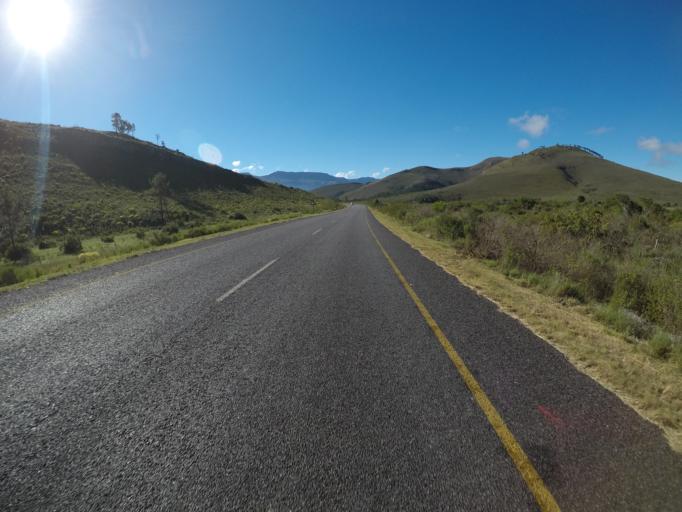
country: ZA
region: Western Cape
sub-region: Overberg District Municipality
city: Caledon
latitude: -34.0802
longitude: 19.5548
